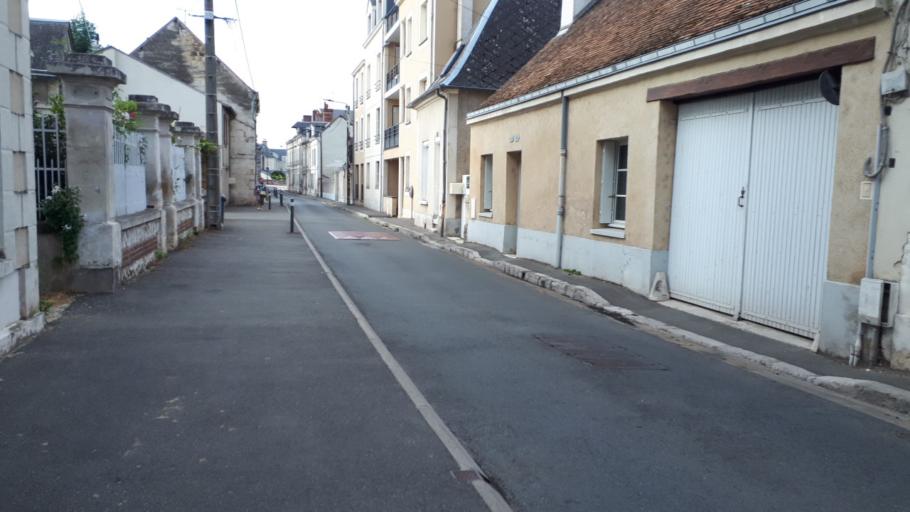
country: FR
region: Centre
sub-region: Departement du Loir-et-Cher
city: Vendome
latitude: 47.7963
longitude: 1.0638
